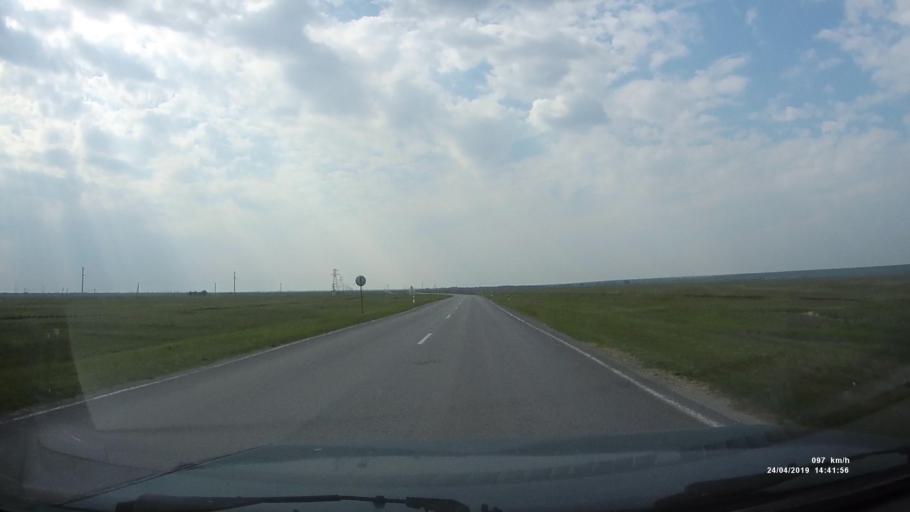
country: RU
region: Rostov
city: Remontnoye
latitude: 46.4492
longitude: 43.8717
